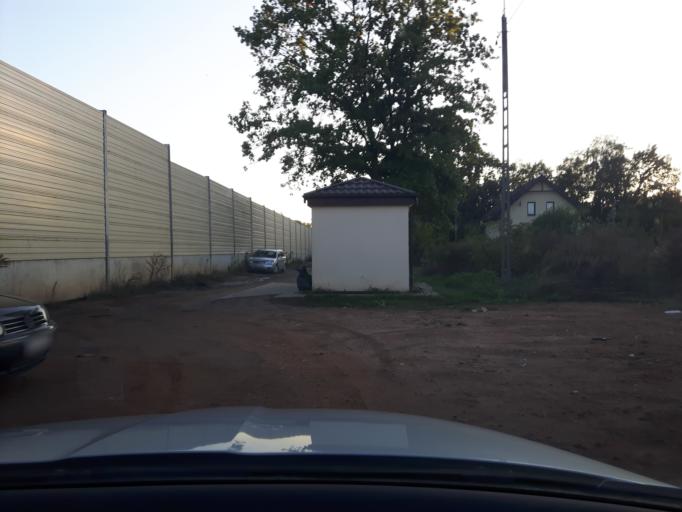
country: PL
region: Masovian Voivodeship
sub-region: Powiat wolominski
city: Kobylka
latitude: 52.3264
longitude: 21.1905
